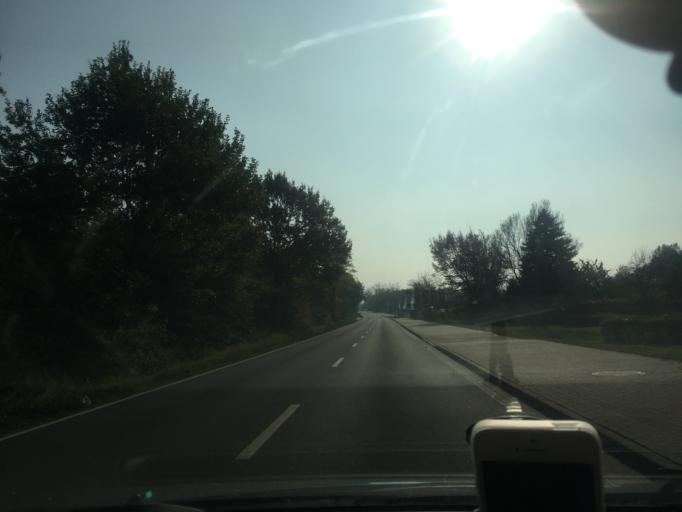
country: DE
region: Mecklenburg-Vorpommern
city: Hagenow
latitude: 53.4309
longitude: 11.1831
